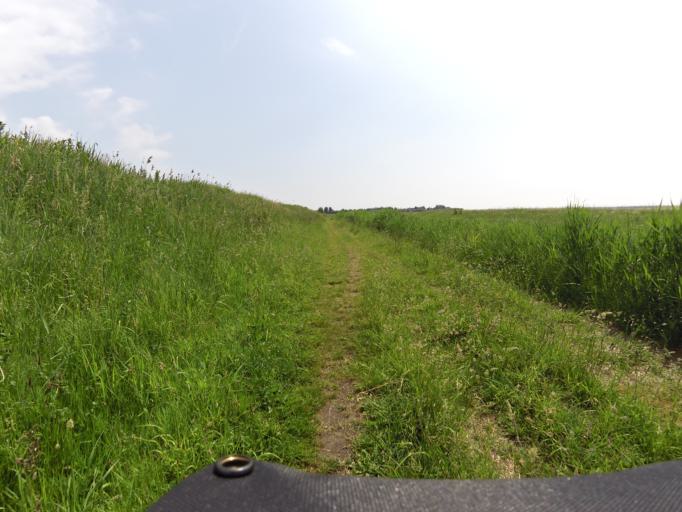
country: NL
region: North Brabant
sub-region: Gemeente Bergen op Zoom
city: Bergen op Zoom
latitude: 51.4850
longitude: 4.2544
